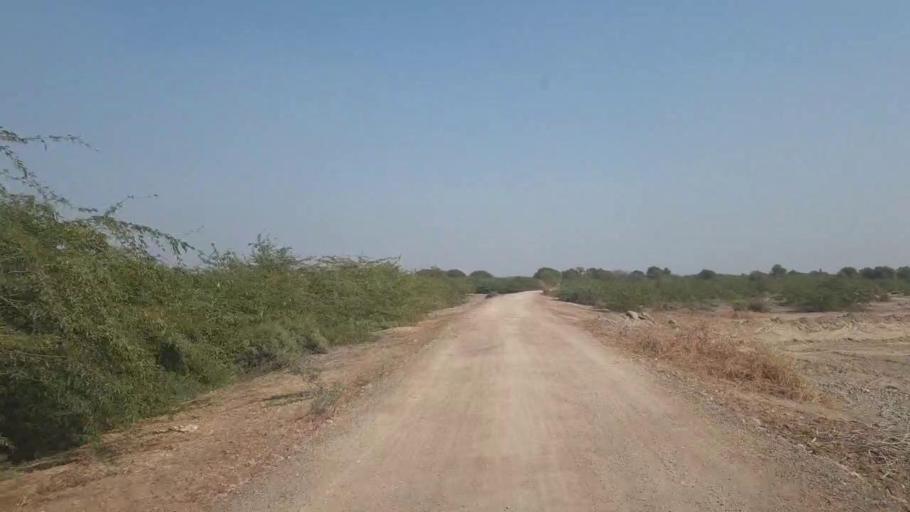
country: PK
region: Sindh
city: Mirpur Khas
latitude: 25.4436
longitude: 68.8934
